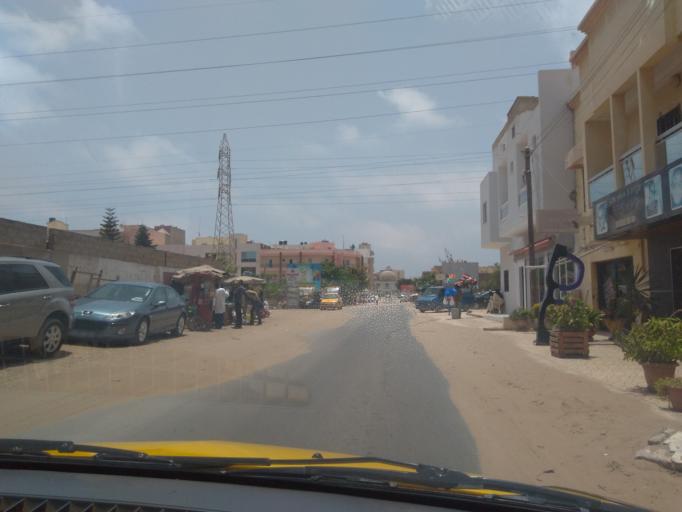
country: SN
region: Dakar
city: Grand Dakar
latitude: 14.7359
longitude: -17.4337
